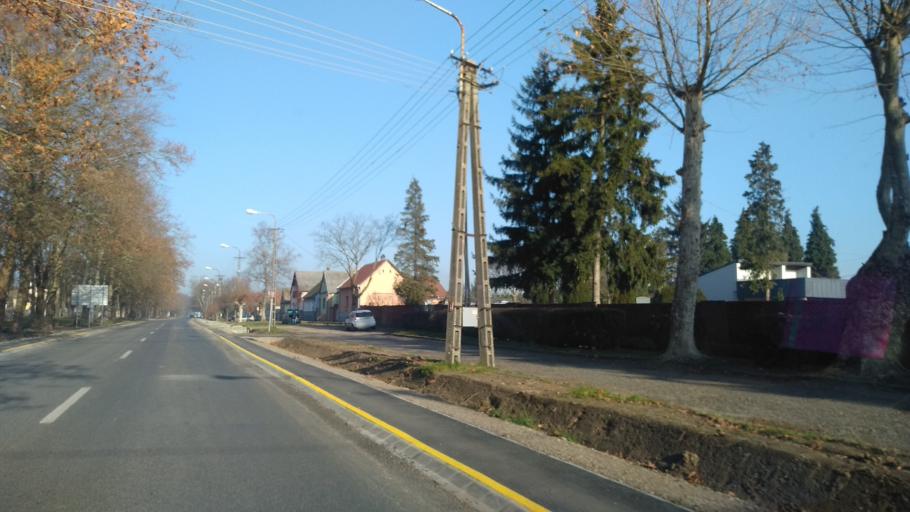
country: HU
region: Somogy
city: Barcs
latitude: 45.9686
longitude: 17.4589
